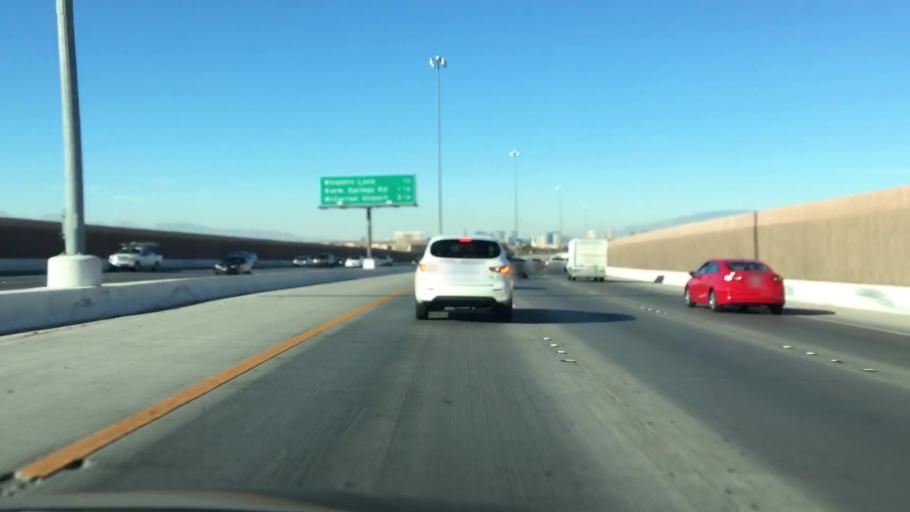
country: US
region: Nevada
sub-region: Clark County
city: Whitney
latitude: 36.0289
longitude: -115.1305
